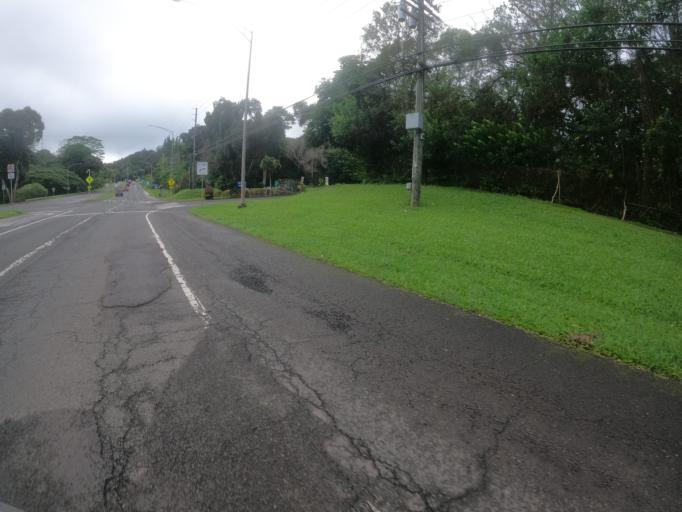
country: US
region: Hawaii
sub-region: Honolulu County
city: Maunawili
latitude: 21.3772
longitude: -157.7833
